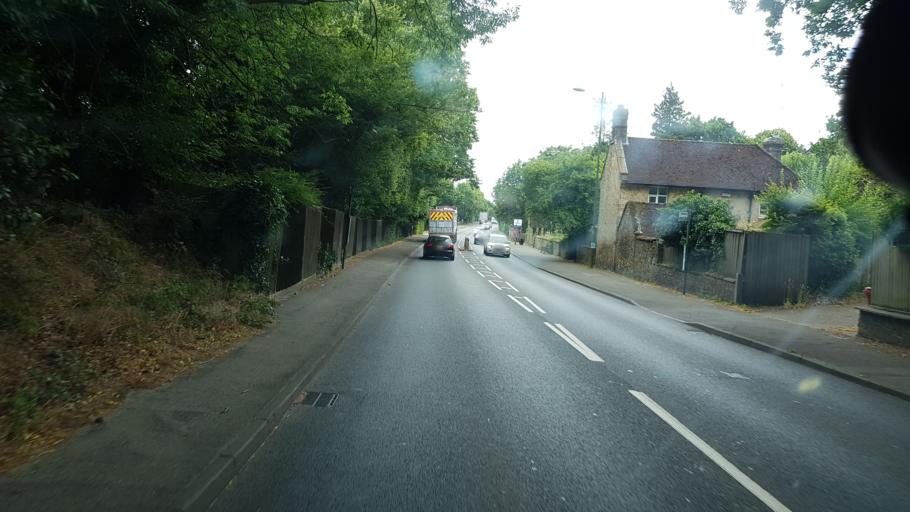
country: GB
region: England
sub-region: Surrey
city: Lingfield
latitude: 51.1969
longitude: -0.0536
